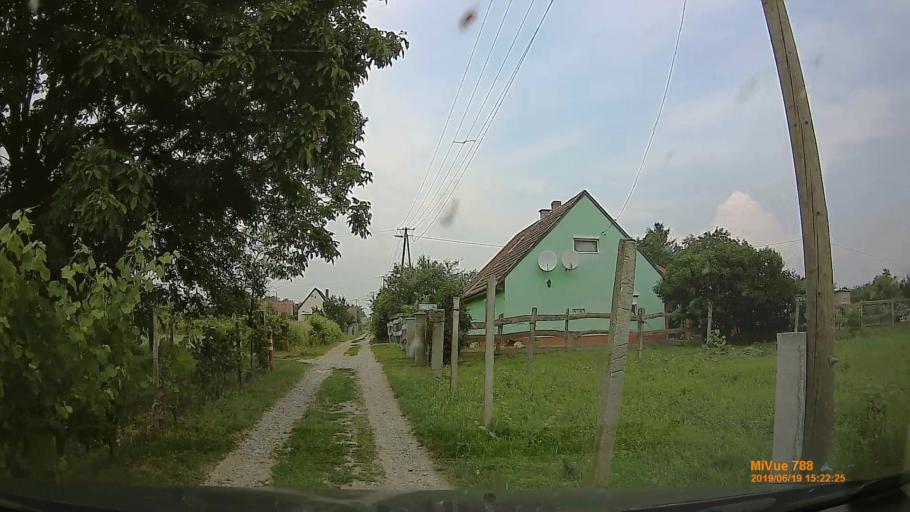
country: HU
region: Baranya
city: Szigetvar
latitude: 46.0735
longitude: 17.8468
